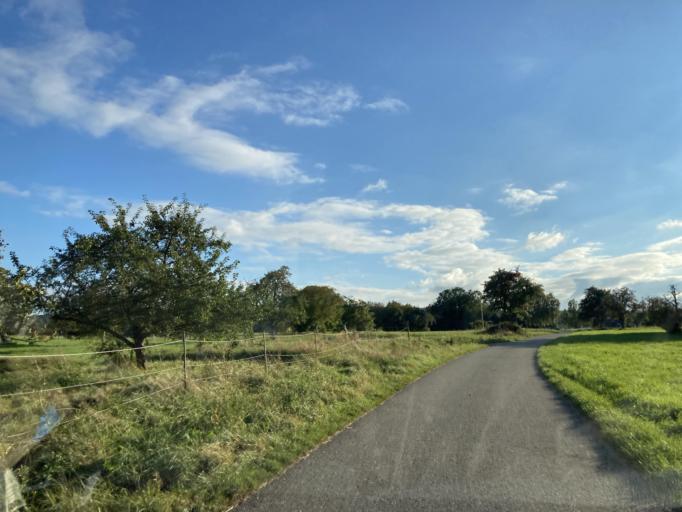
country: DE
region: Baden-Wuerttemberg
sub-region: Karlsruhe Region
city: Dobel
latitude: 48.8476
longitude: 8.5075
